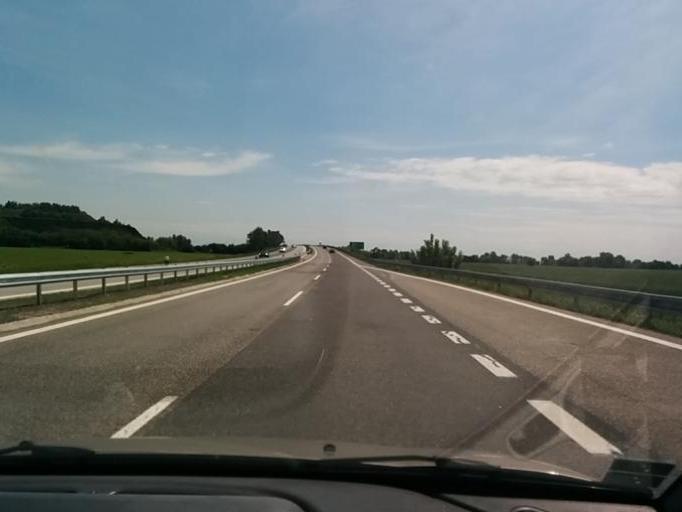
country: SK
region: Trnavsky
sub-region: Okres Galanta
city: Galanta
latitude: 48.2672
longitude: 17.7235
